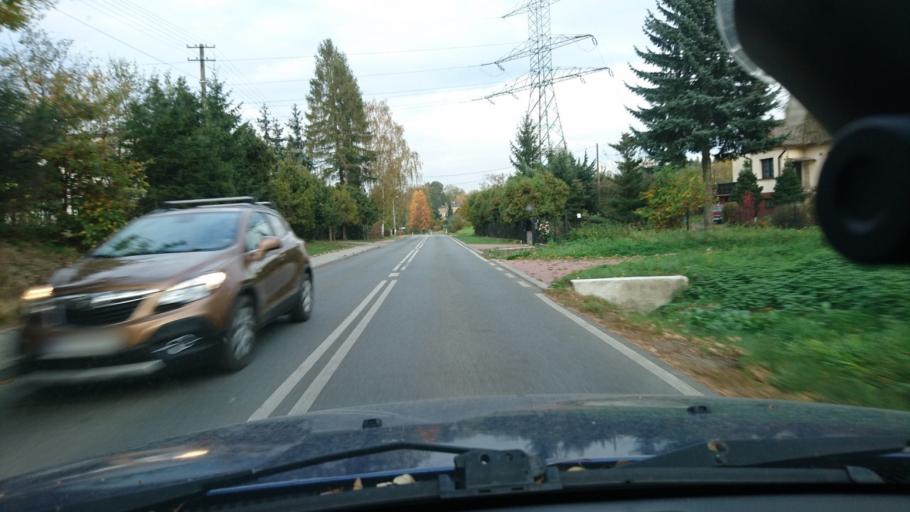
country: PL
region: Silesian Voivodeship
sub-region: Powiat bielski
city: Kozy
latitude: 49.8571
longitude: 19.1438
